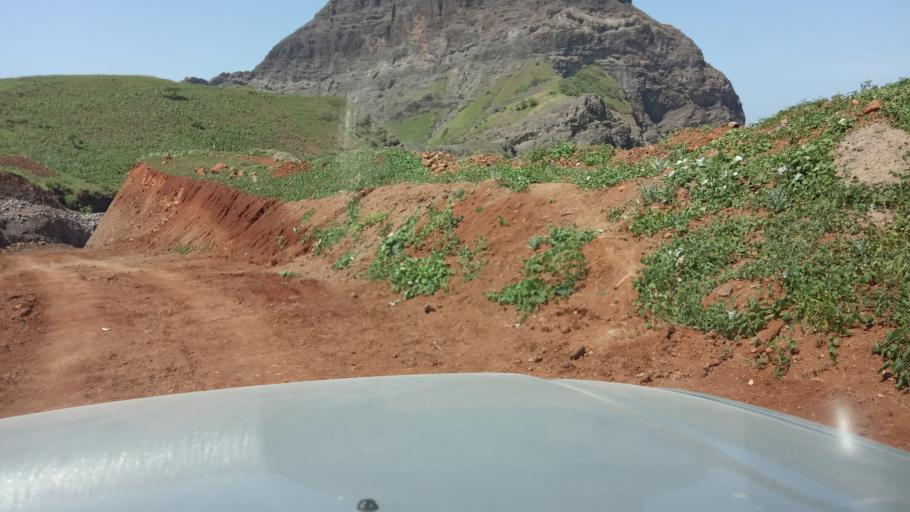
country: CV
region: Santa Catarina
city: Assomada
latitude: 15.1092
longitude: -23.7290
